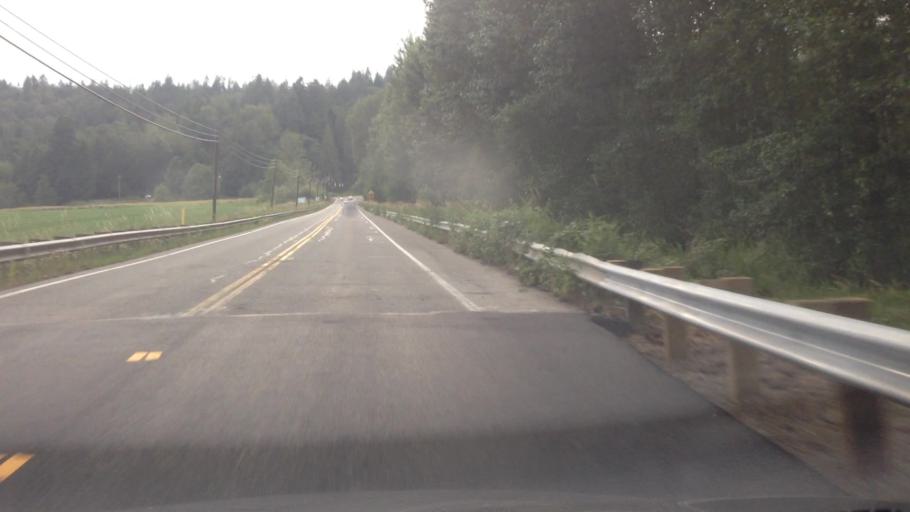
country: US
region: Washington
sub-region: King County
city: Duvall
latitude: 47.7438
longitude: -122.0032
